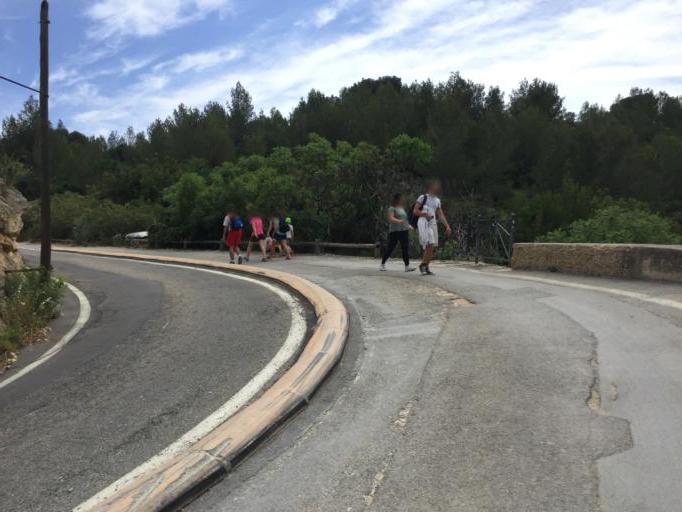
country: FR
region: Provence-Alpes-Cote d'Azur
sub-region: Departement des Bouches-du-Rhone
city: Cassis
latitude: 43.2116
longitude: 5.5220
